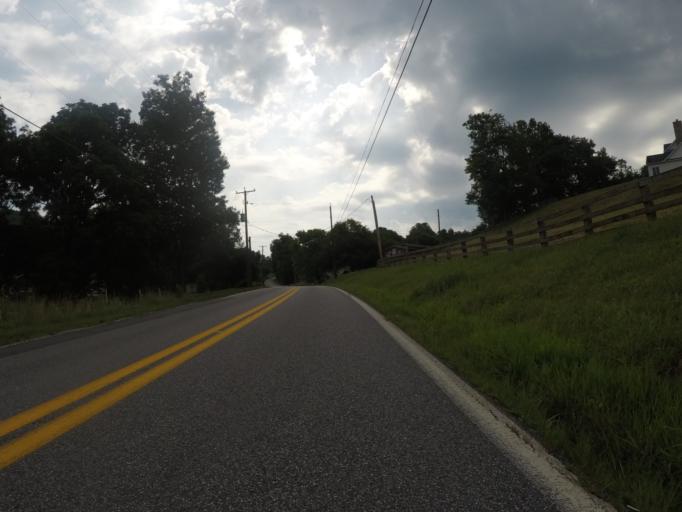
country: US
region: West Virginia
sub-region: Cabell County
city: Barboursville
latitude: 38.3814
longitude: -82.2652
